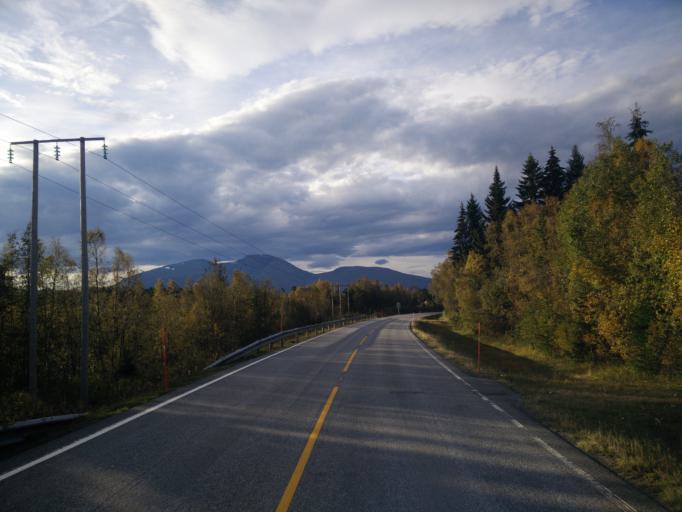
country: NO
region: More og Romsdal
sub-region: Gjemnes
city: Batnfjordsora
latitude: 62.8263
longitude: 7.6047
